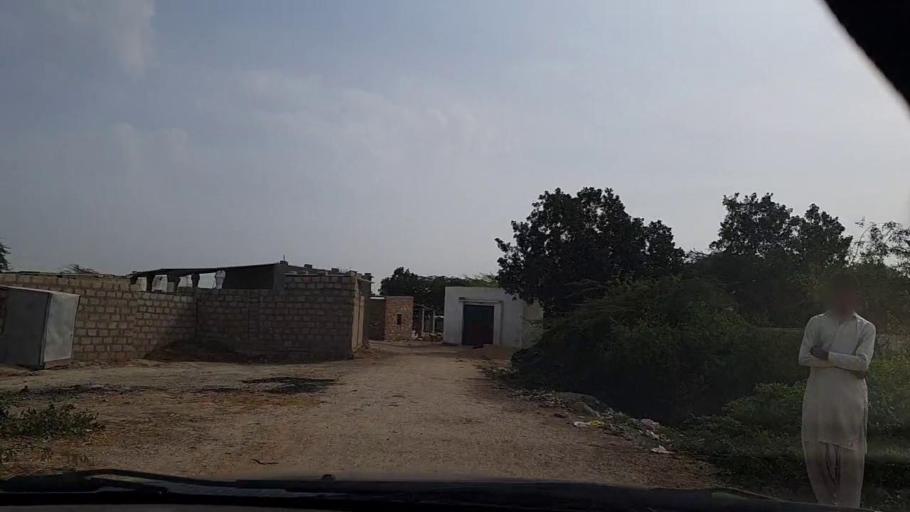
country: PK
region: Sindh
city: Thatta
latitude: 24.5770
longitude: 67.8880
